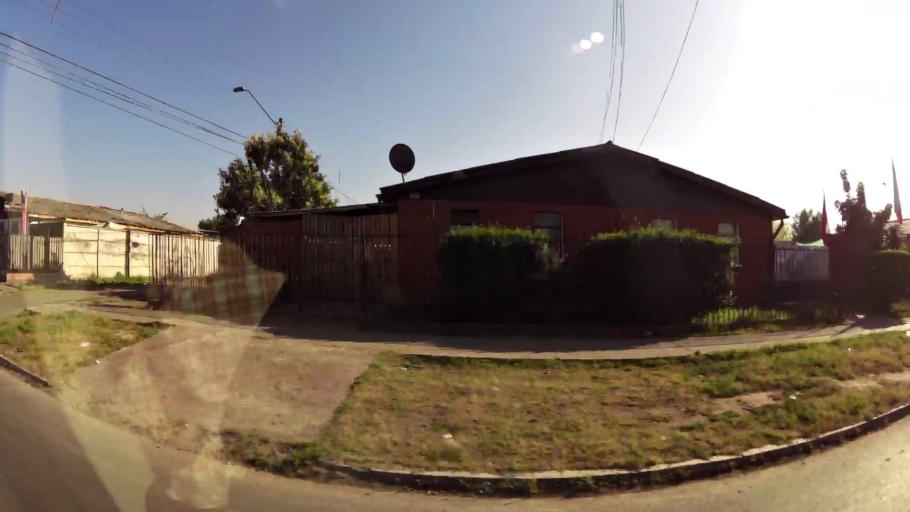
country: CL
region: Santiago Metropolitan
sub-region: Provincia de Santiago
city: Santiago
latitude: -33.3841
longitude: -70.6599
